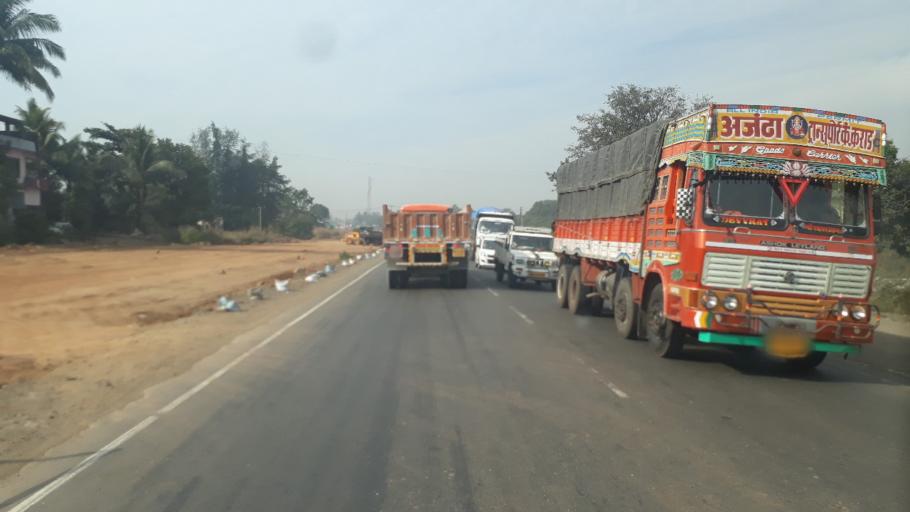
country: IN
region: Maharashtra
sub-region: Raigarh
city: Pen
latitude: 18.7264
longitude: 73.0747
